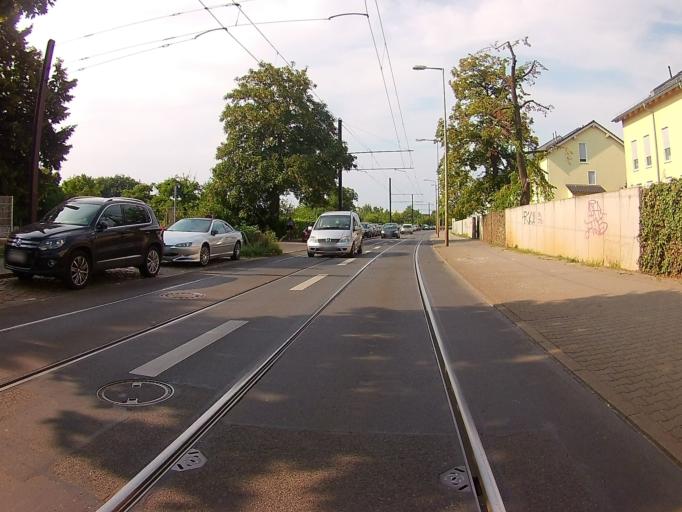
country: DE
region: Berlin
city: Kopenick Bezirk
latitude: 52.4317
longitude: 13.5715
